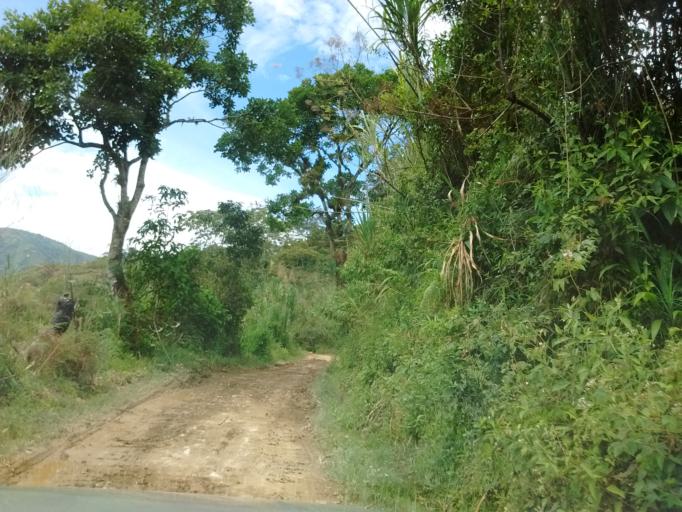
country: CO
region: Cauca
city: Morales
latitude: 2.6788
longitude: -76.7631
